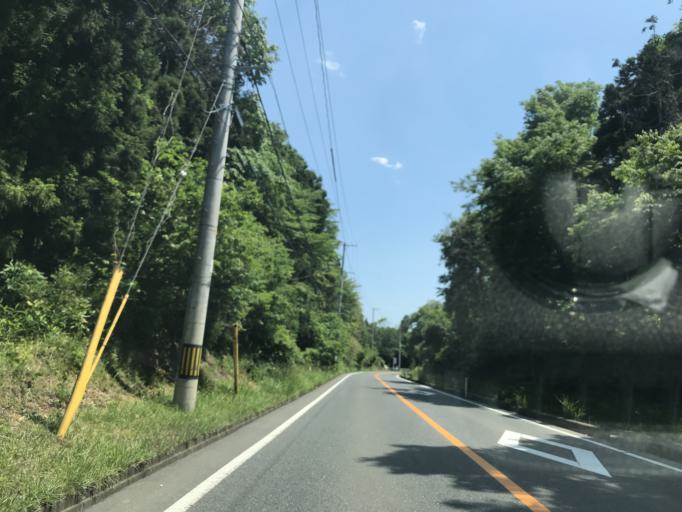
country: JP
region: Miyagi
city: Matsushima
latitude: 38.3859
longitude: 141.1137
